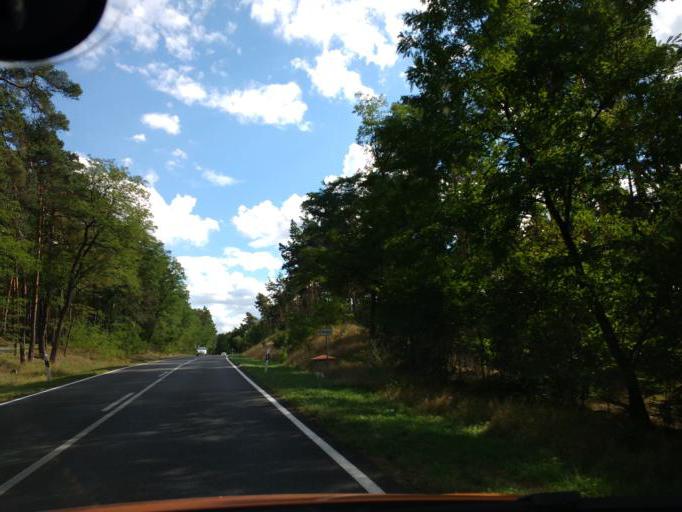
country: DE
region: Brandenburg
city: Wendisch Rietz
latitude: 52.2173
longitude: 13.9844
